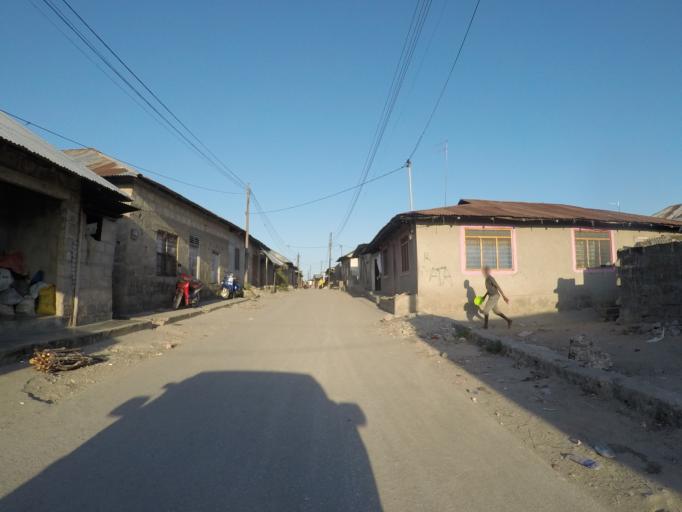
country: TZ
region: Zanzibar Urban/West
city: Zanzibar
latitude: -6.1578
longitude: 39.2117
